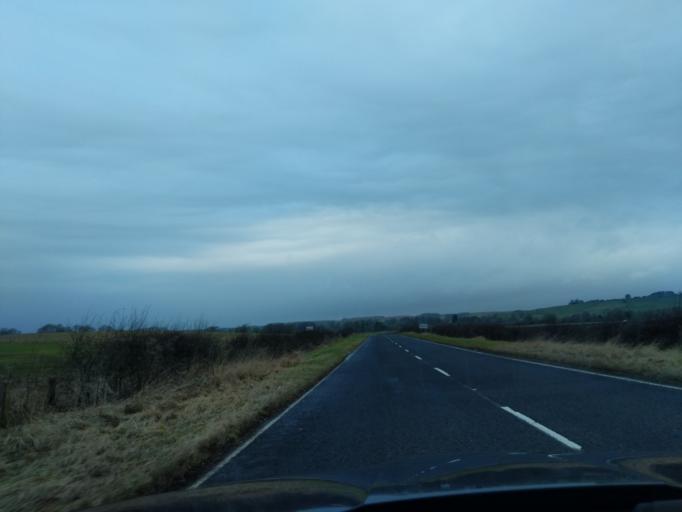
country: GB
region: England
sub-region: Northumberland
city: Rothley
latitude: 55.1474
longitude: -1.9953
